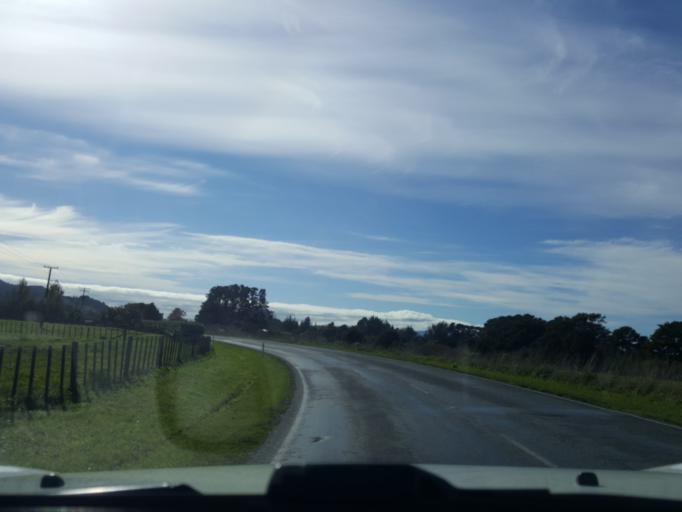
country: NZ
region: Waikato
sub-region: Waikato District
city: Ngaruawahia
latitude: -37.6090
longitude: 175.1969
